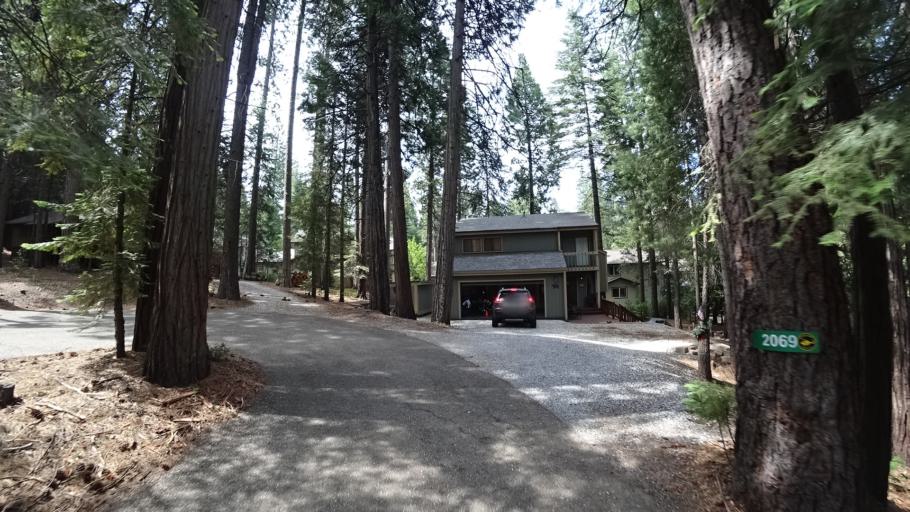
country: US
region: California
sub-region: Calaveras County
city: Arnold
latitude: 38.2417
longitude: -120.3590
